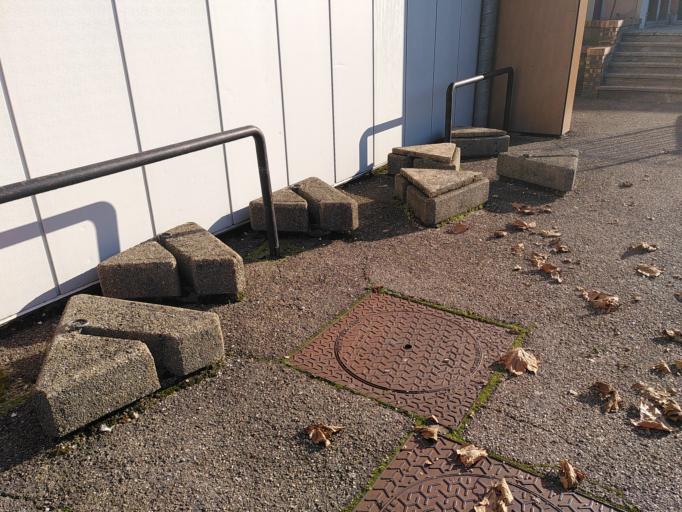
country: FR
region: Lorraine
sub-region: Departement de Meurthe-et-Moselle
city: Pont-a-Mousson
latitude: 48.9161
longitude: 6.0577
